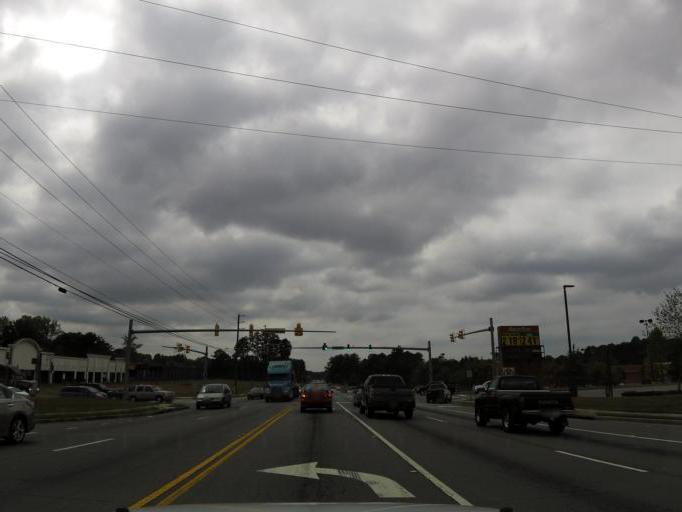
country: US
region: Georgia
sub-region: Cobb County
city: Powder Springs
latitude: 33.8665
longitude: -84.6330
